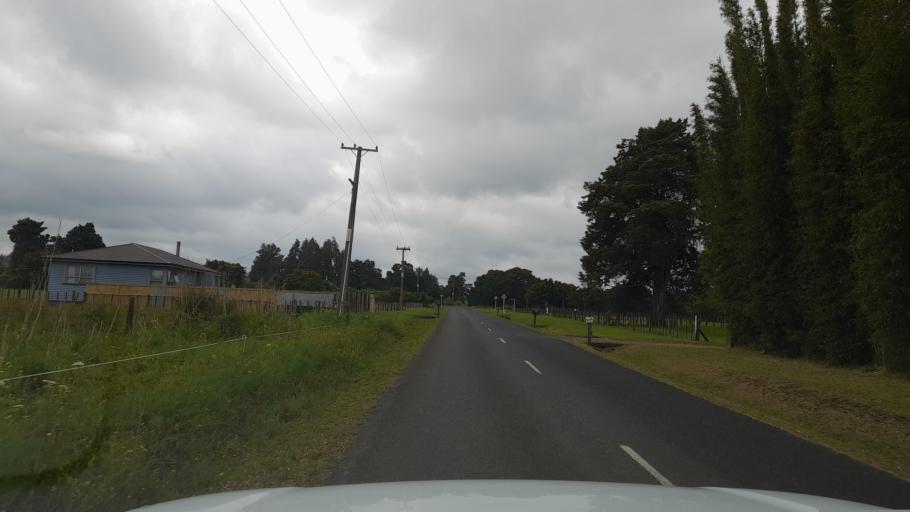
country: NZ
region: Northland
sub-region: Far North District
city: Waimate North
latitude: -35.4205
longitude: 173.7951
